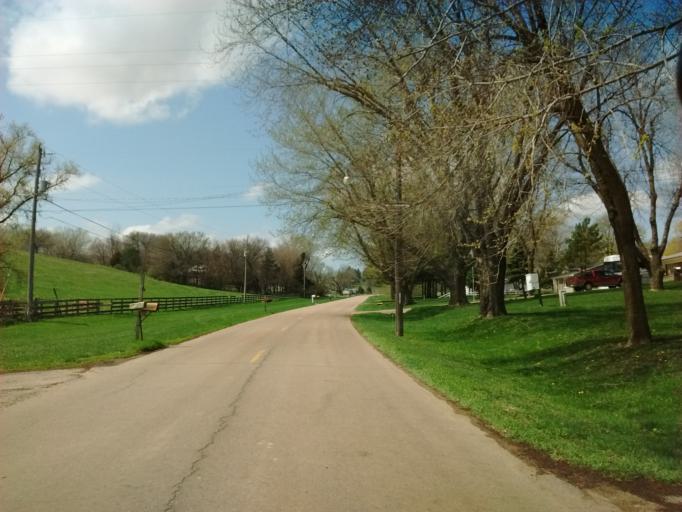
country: US
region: South Dakota
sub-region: Union County
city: North Sioux City
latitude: 42.5512
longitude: -96.4485
